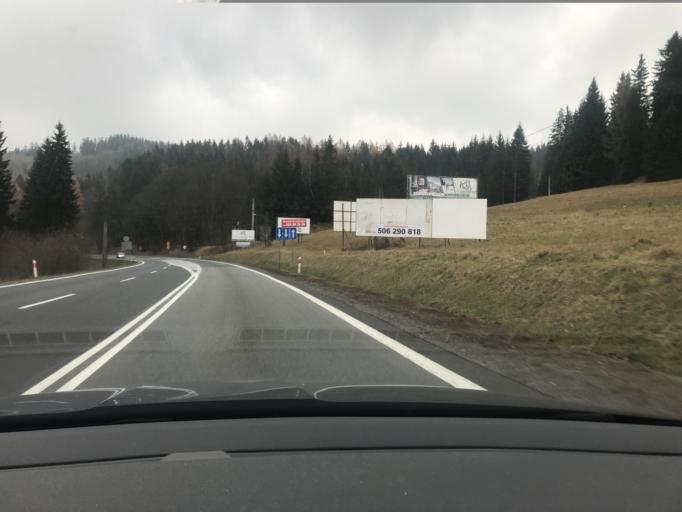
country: PL
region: Lower Silesian Voivodeship
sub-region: Powiat klodzki
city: Duszniki-Zdroj
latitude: 50.3939
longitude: 16.3612
